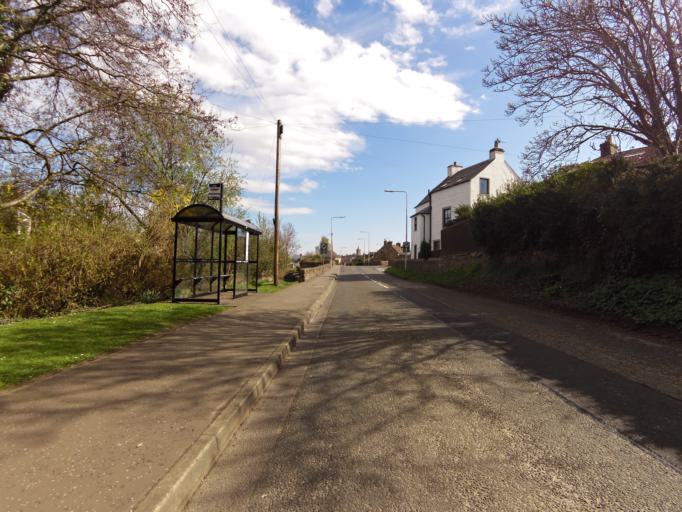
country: GB
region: Scotland
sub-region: Fife
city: Auchtermuchty
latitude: 56.2954
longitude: -3.2368
